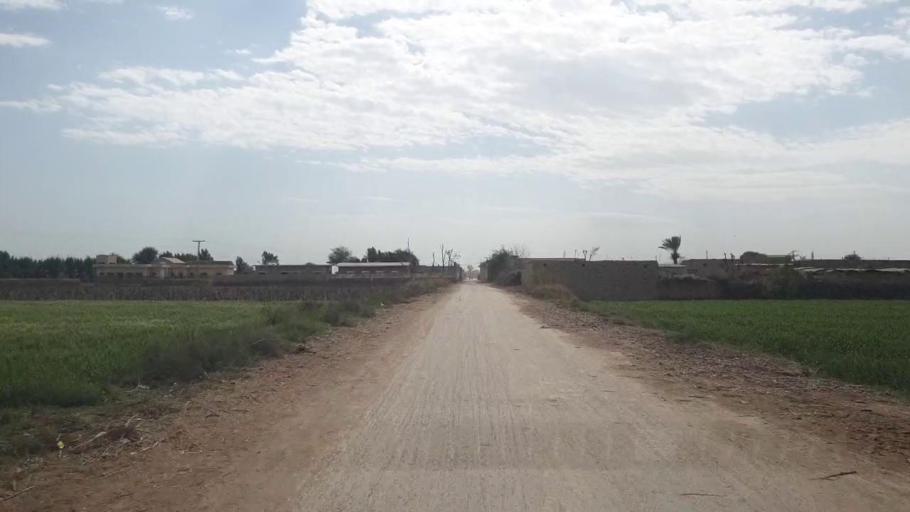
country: PK
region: Sindh
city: Hala
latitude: 25.9437
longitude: 68.4298
